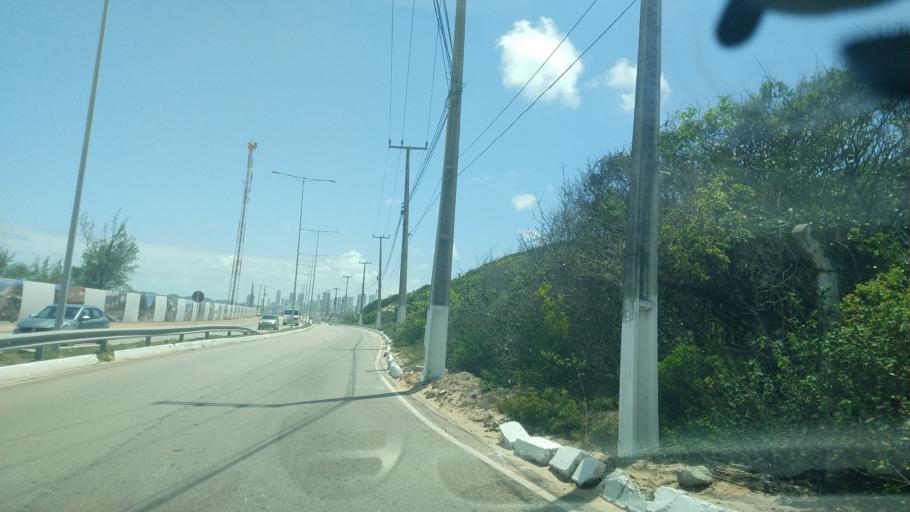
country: BR
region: Rio Grande do Norte
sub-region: Natal
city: Natal
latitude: -5.8434
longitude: -35.1829
